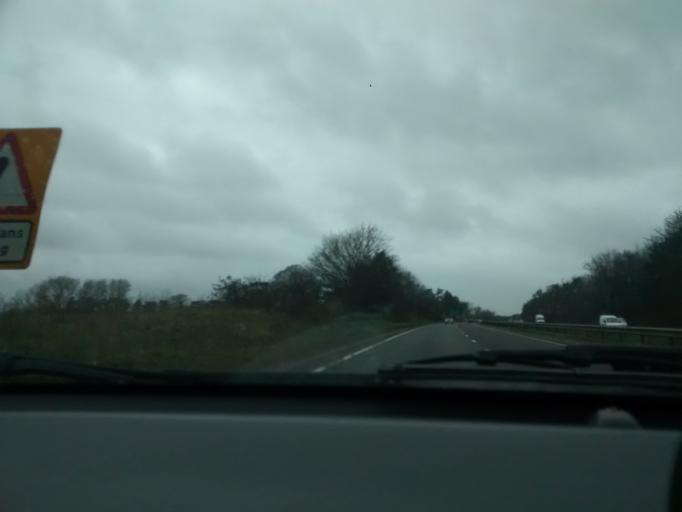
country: GB
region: England
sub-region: Suffolk
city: Needham Market
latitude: 52.1323
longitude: 1.0923
